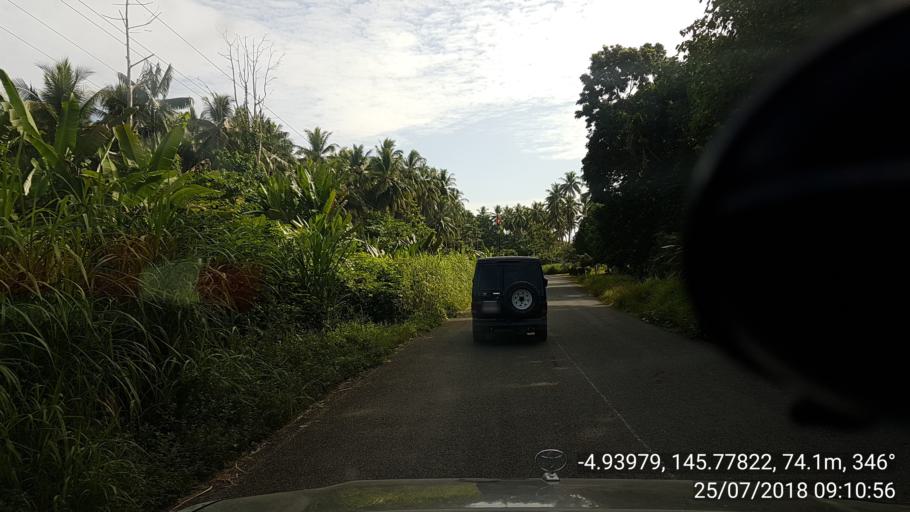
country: PG
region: Madang
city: Madang
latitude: -4.9397
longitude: 145.7783
